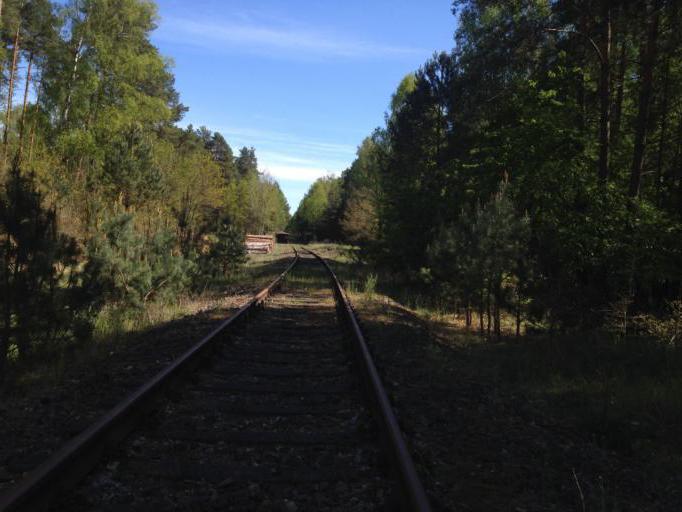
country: DE
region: Brandenburg
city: Lychen
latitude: 53.1529
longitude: 13.3962
